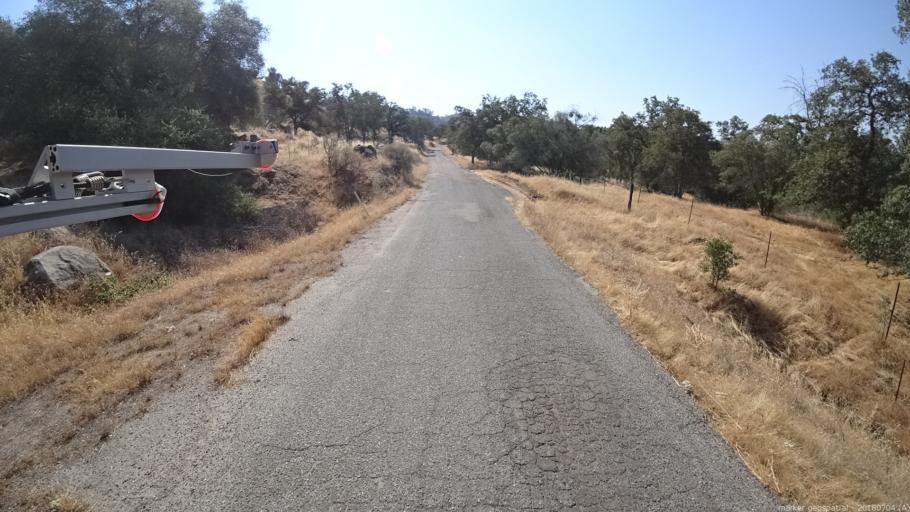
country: US
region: California
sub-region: Fresno County
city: Auberry
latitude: 37.1067
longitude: -119.6298
